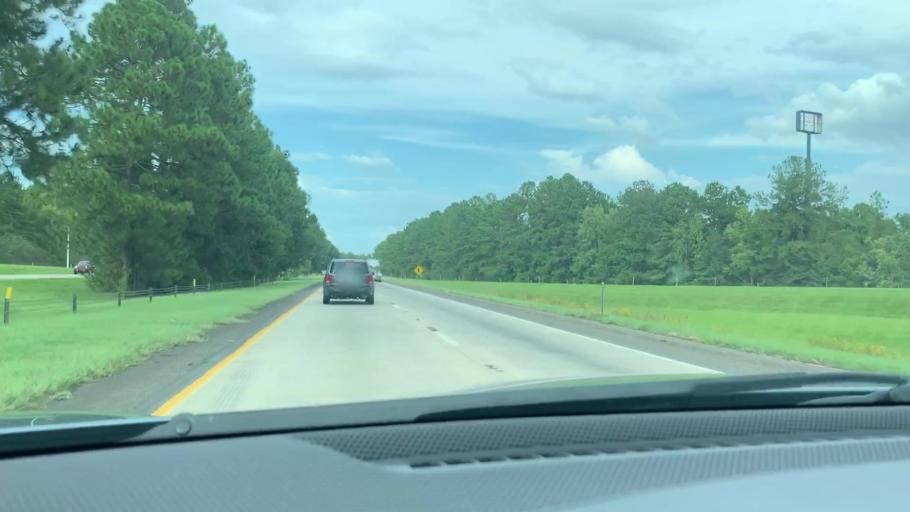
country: US
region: South Carolina
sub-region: Colleton County
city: Walterboro
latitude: 32.8804
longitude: -80.7160
